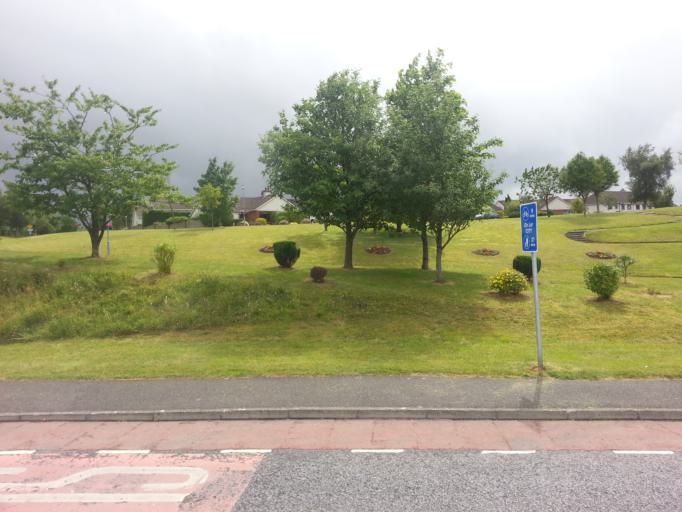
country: IE
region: Leinster
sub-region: Kilkenny
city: Kilkenny
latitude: 52.6427
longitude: -7.2329
